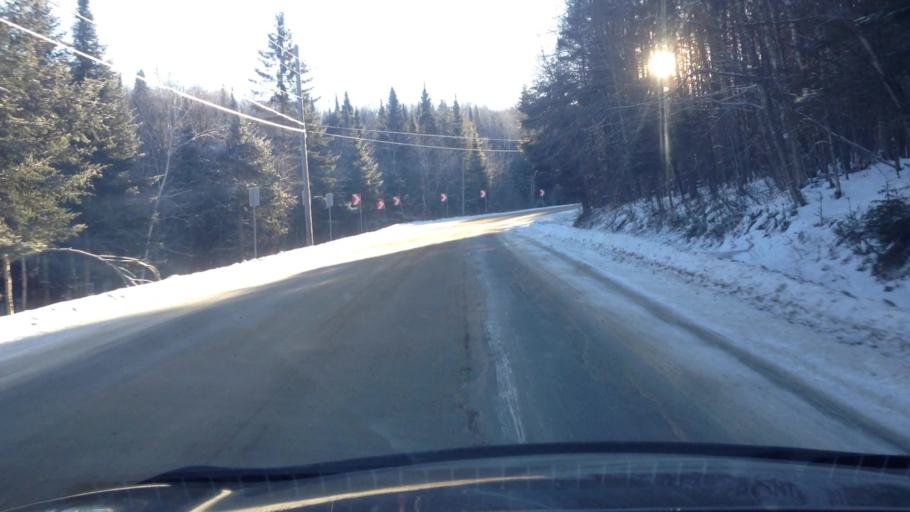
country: CA
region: Quebec
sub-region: Laurentides
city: Brownsburg-Chatham
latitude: 45.9307
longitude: -74.5438
